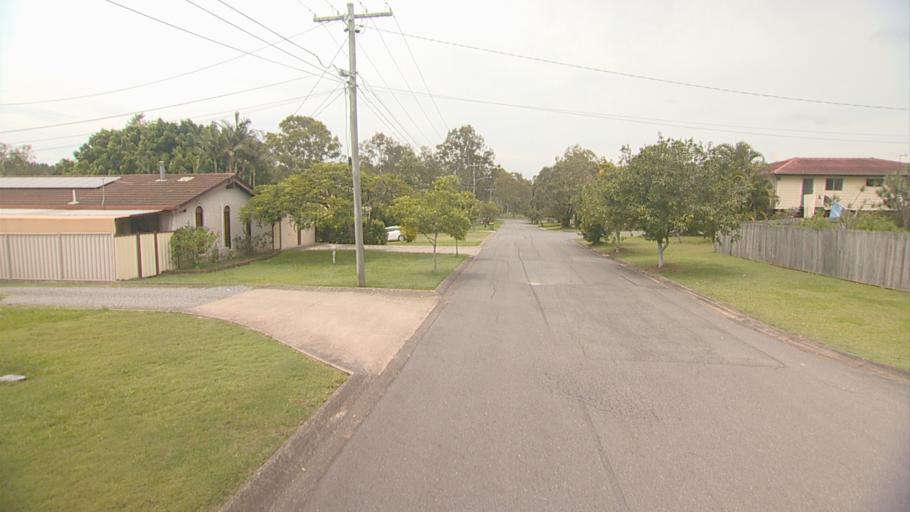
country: AU
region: Queensland
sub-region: Logan
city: Slacks Creek
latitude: -27.6489
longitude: 153.1505
